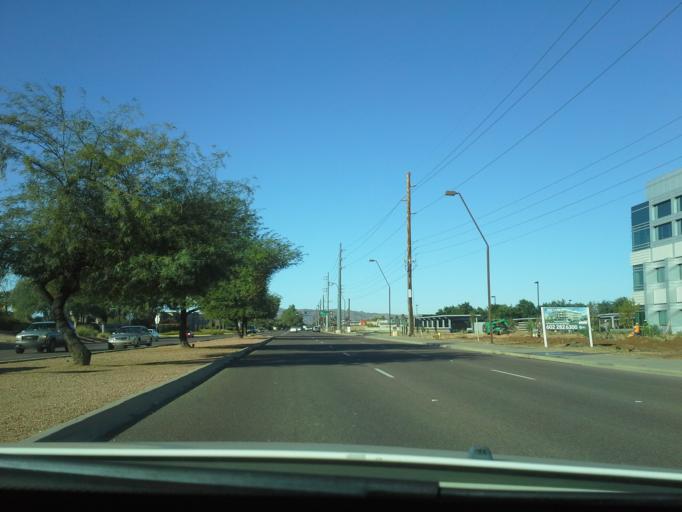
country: US
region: Arizona
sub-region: Maricopa County
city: San Carlos
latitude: 33.3494
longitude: -111.8957
